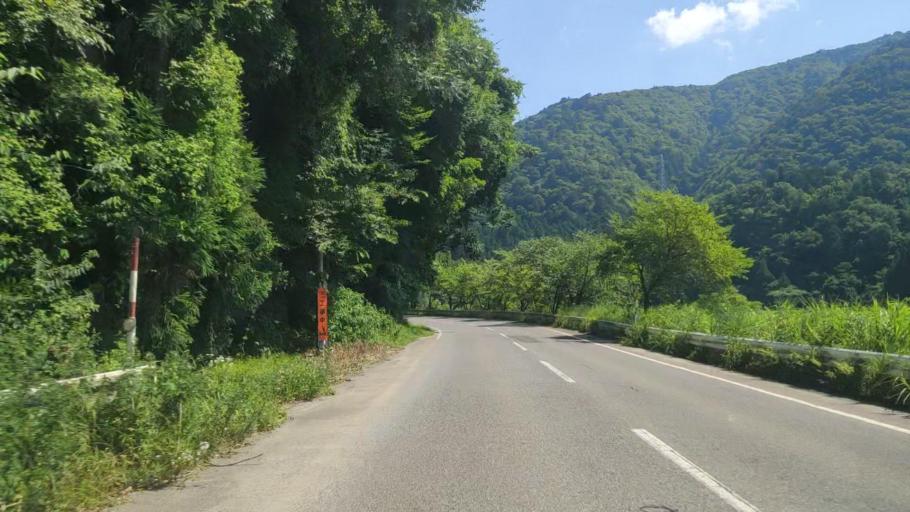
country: JP
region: Gifu
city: Godo
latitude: 35.6157
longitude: 136.6231
